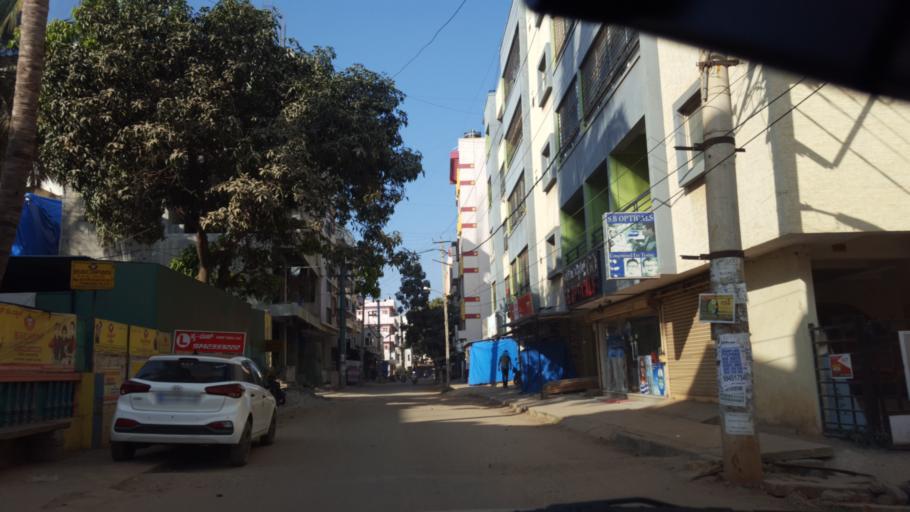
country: IN
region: Karnataka
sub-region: Bangalore Urban
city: Bangalore
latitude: 12.9492
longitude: 77.7092
